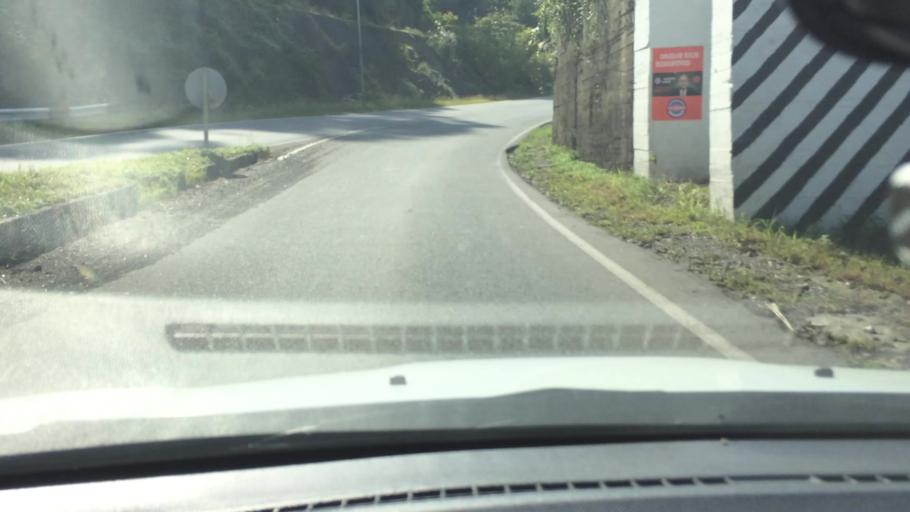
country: GE
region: Ajaria
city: Kobuleti
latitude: 41.7718
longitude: 41.7563
